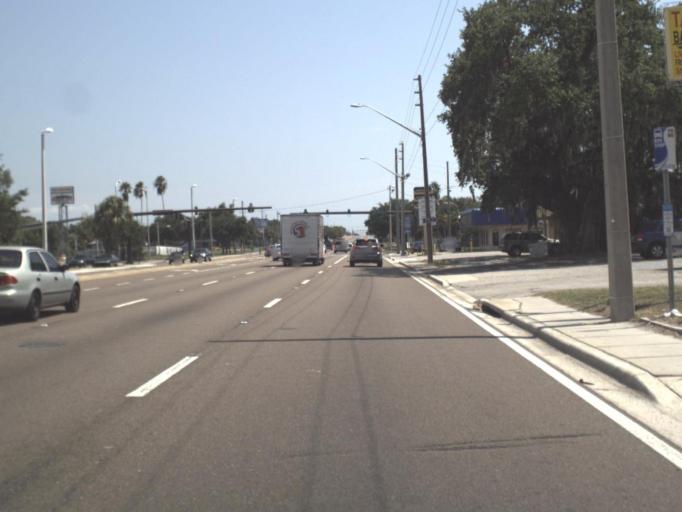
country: US
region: Florida
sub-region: Pinellas County
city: Gulfport
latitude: 27.7460
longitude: -82.6794
